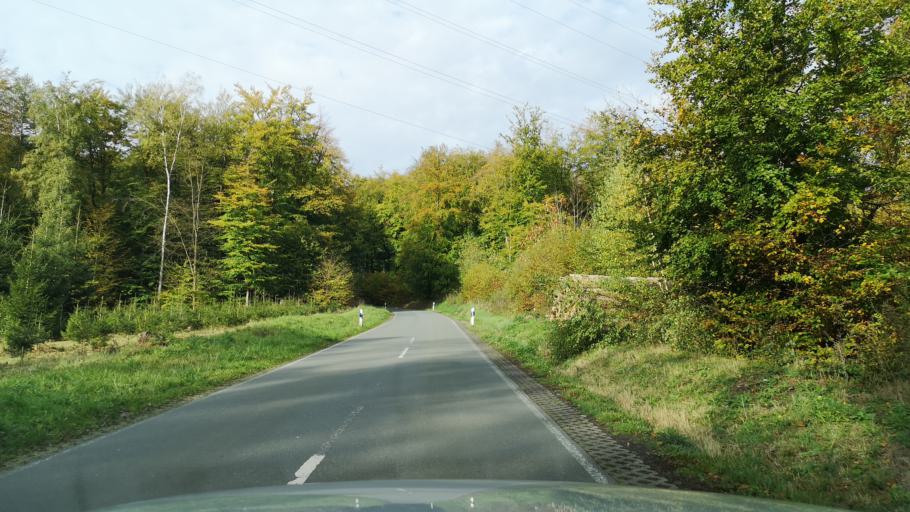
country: DE
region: North Rhine-Westphalia
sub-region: Regierungsbezirk Arnsberg
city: Menden
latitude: 51.4386
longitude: 7.8349
